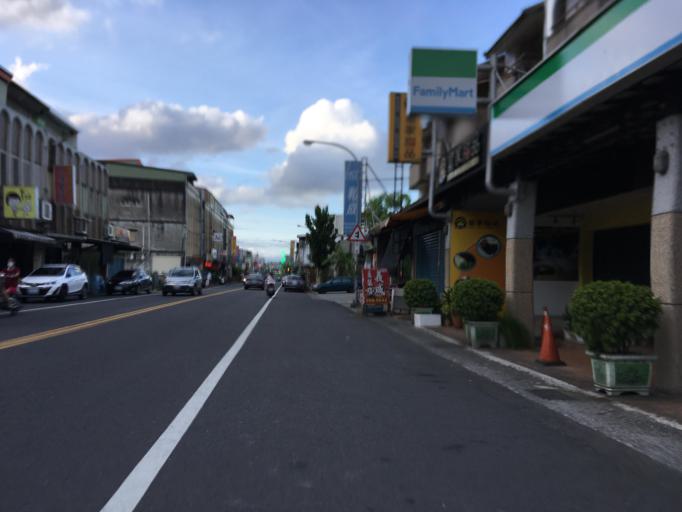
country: TW
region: Taiwan
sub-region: Yilan
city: Yilan
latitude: 24.6629
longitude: 121.7667
